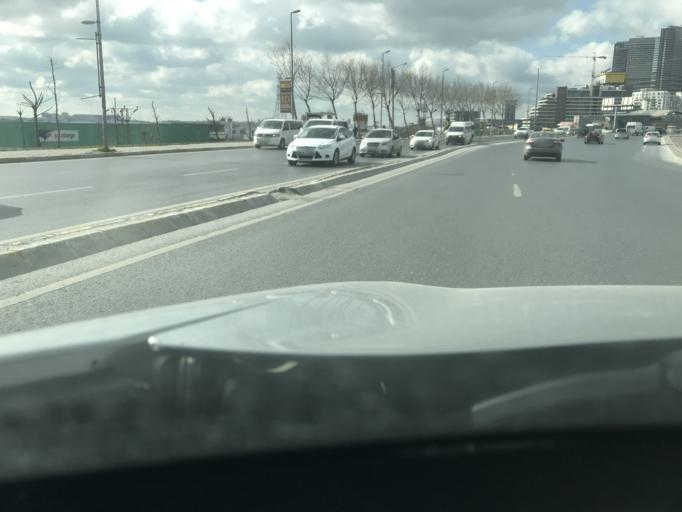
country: TR
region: Istanbul
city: Esenyurt
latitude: 41.0519
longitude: 28.6713
